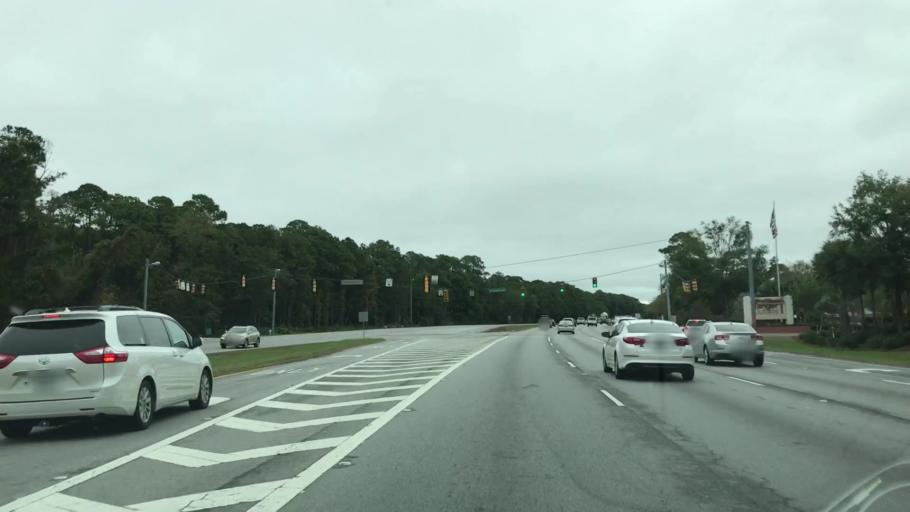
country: US
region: South Carolina
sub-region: Beaufort County
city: Bluffton
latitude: 32.2478
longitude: -80.8329
